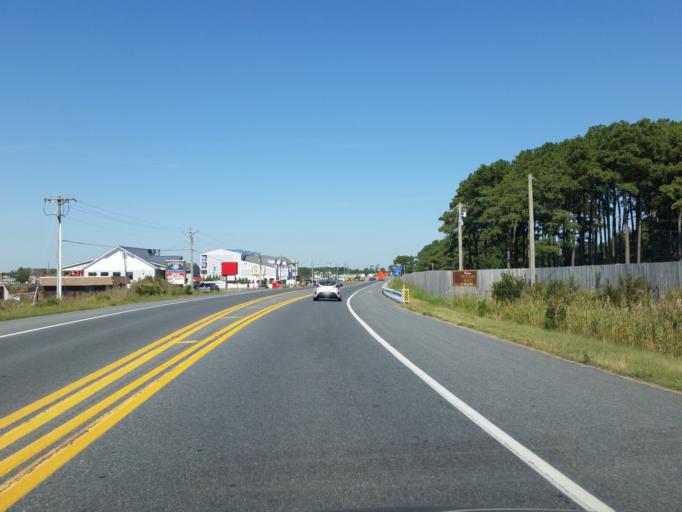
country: US
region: Delaware
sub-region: Sussex County
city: Bethany Beach
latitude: 38.4597
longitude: -75.0766
